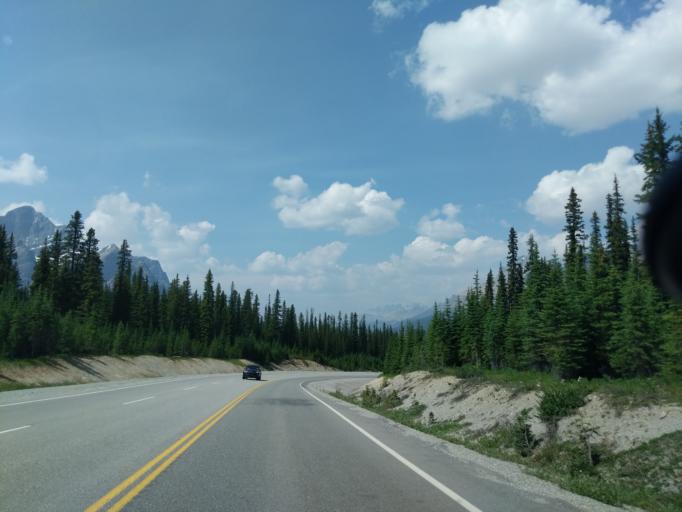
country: CA
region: Alberta
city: Lake Louise
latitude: 51.7241
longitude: -116.4997
